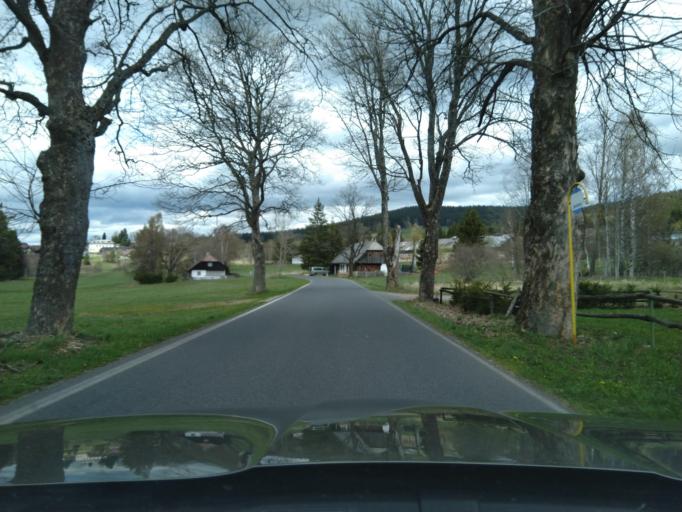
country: CZ
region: Jihocesky
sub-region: Okres Prachatice
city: Borova Lada
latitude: 49.0018
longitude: 13.6719
